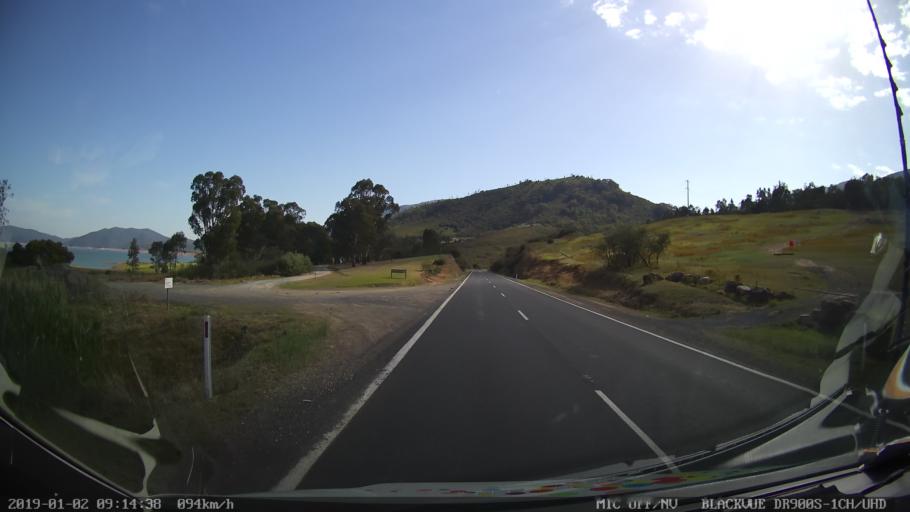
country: AU
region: New South Wales
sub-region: Tumut Shire
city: Tumut
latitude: -35.4747
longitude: 148.2757
